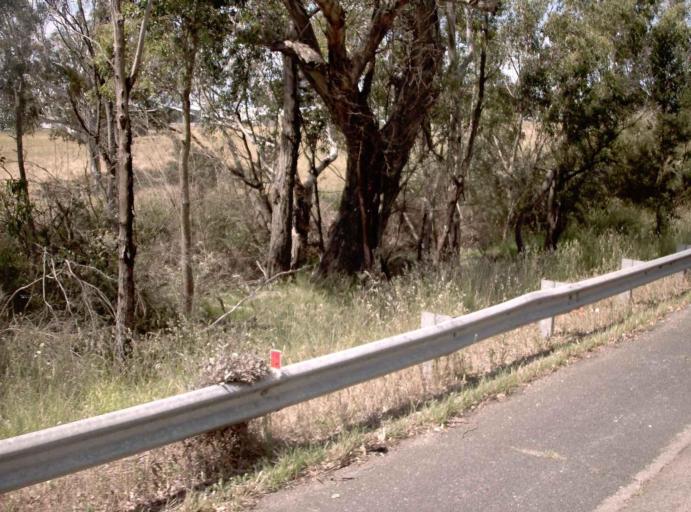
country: AU
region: Victoria
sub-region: Wellington
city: Sale
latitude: -37.9292
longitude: 147.2055
